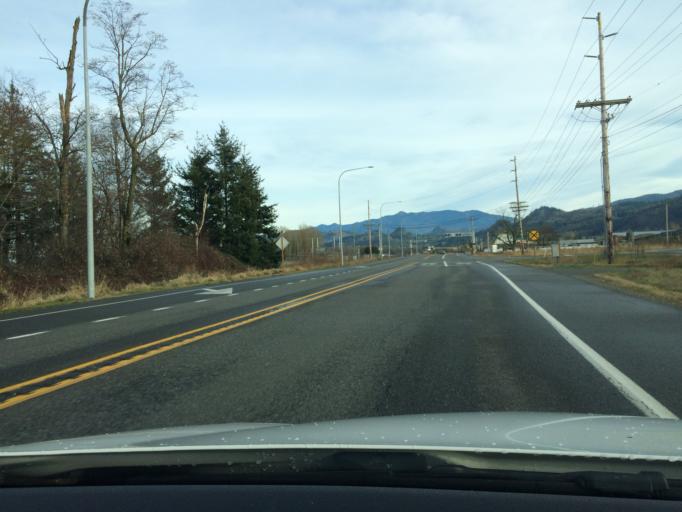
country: US
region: Washington
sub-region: Whatcom County
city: Sumas
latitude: 48.9639
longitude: -122.2899
